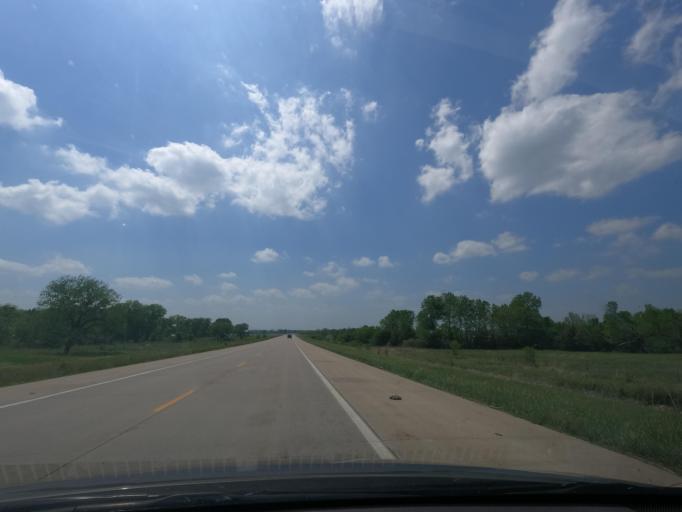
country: US
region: Kansas
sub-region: Wilson County
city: Fredonia
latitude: 37.6195
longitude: -96.0237
